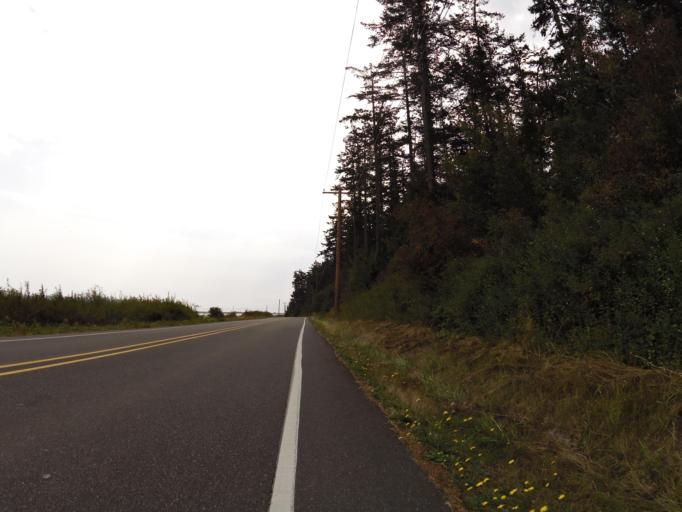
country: US
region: Washington
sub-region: Island County
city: Coupeville
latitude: 48.1835
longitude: -122.6693
